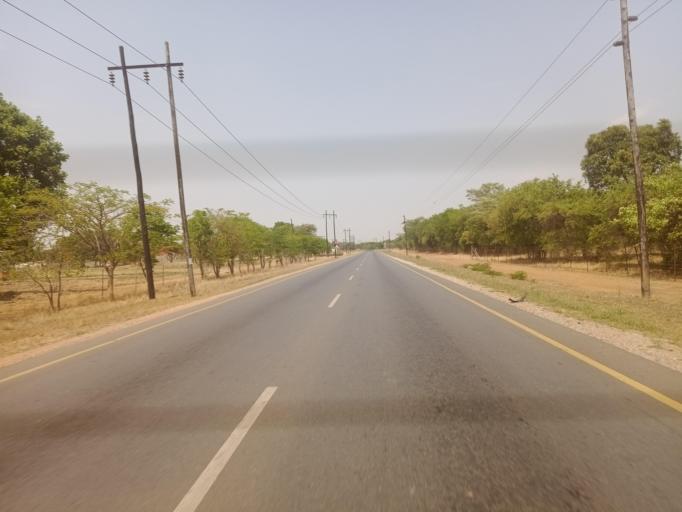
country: ZM
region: Lusaka
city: Lusaka
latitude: -15.2803
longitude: 28.3941
